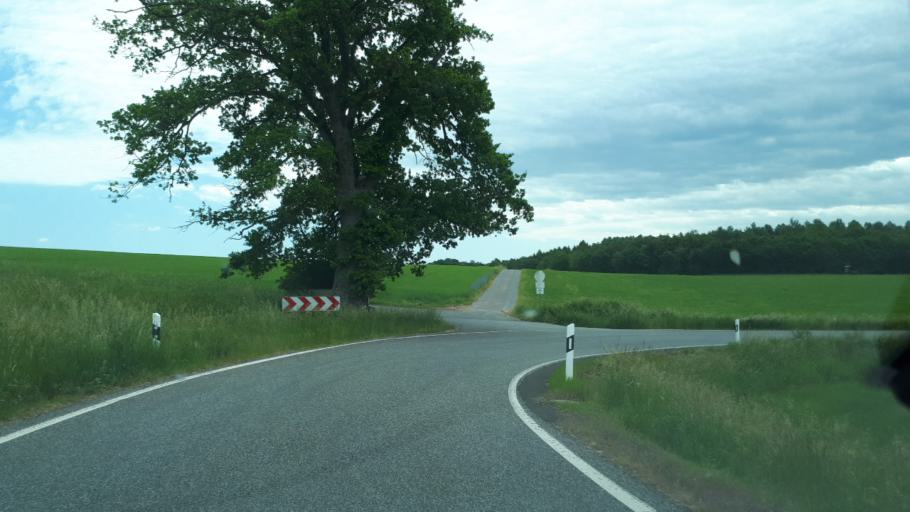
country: DE
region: Rheinland-Pfalz
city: Filz
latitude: 50.1697
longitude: 6.9878
